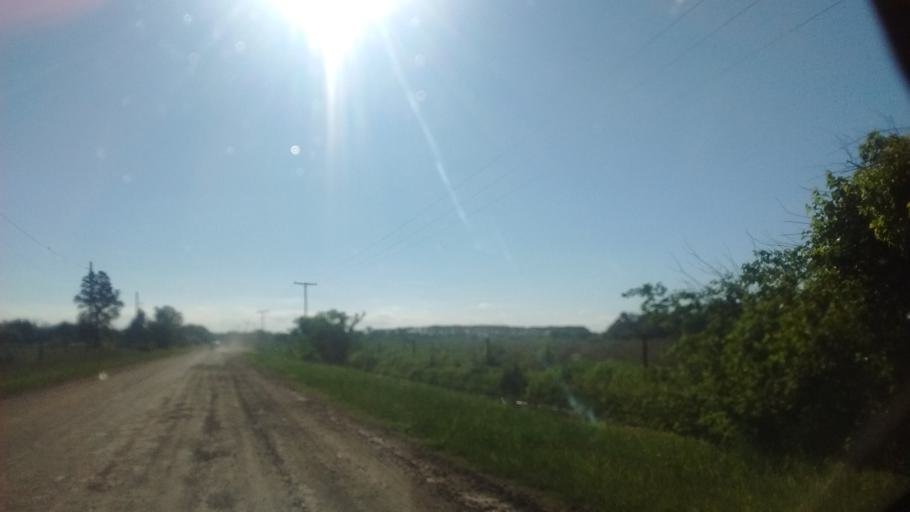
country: AR
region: Santa Fe
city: Funes
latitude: -32.8608
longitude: -60.7978
